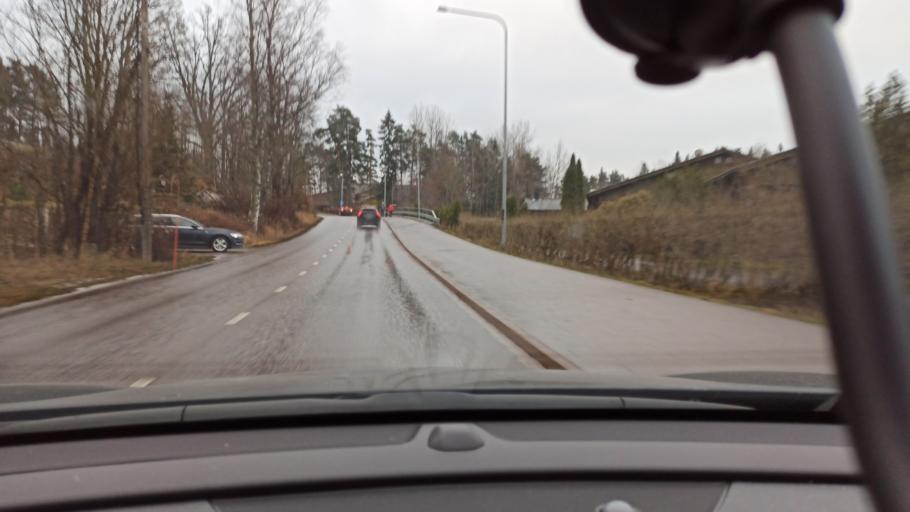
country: FI
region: Uusimaa
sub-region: Helsinki
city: Kirkkonummi
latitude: 60.1318
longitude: 24.4307
